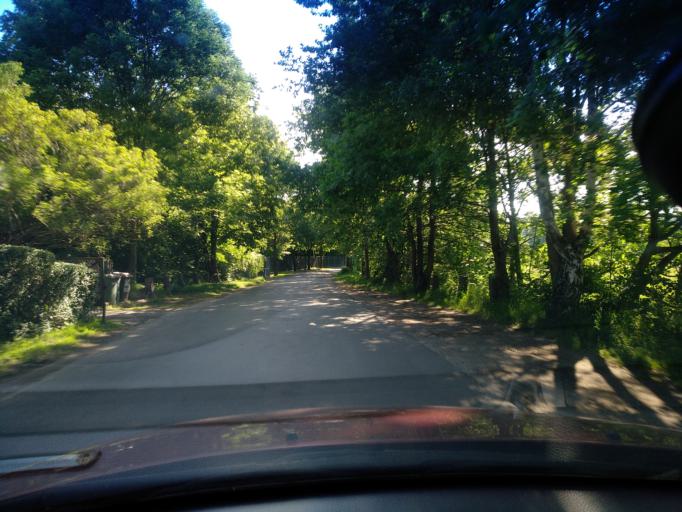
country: PL
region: Lower Silesian Voivodeship
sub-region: Powiat zgorzelecki
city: Zgorzelec
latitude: 51.1351
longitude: 15.0063
